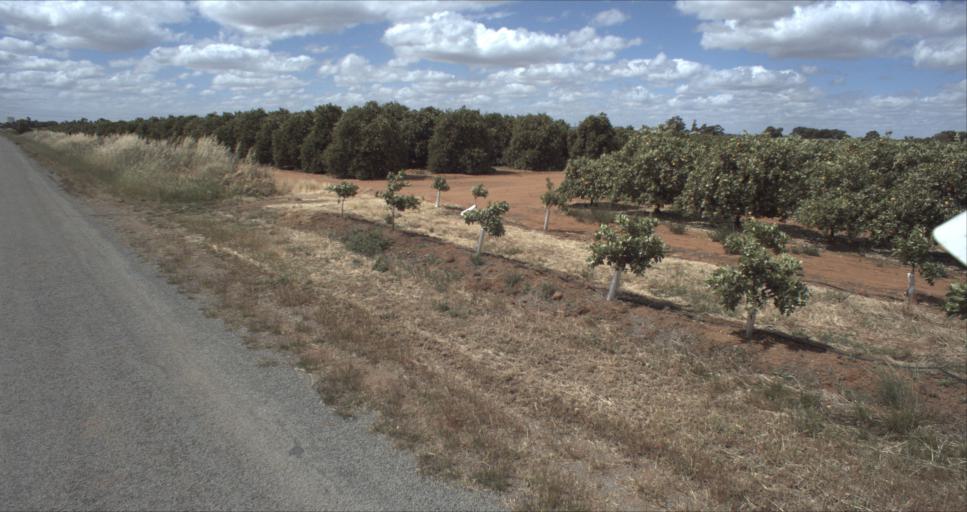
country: AU
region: New South Wales
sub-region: Leeton
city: Leeton
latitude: -34.5826
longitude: 146.3920
